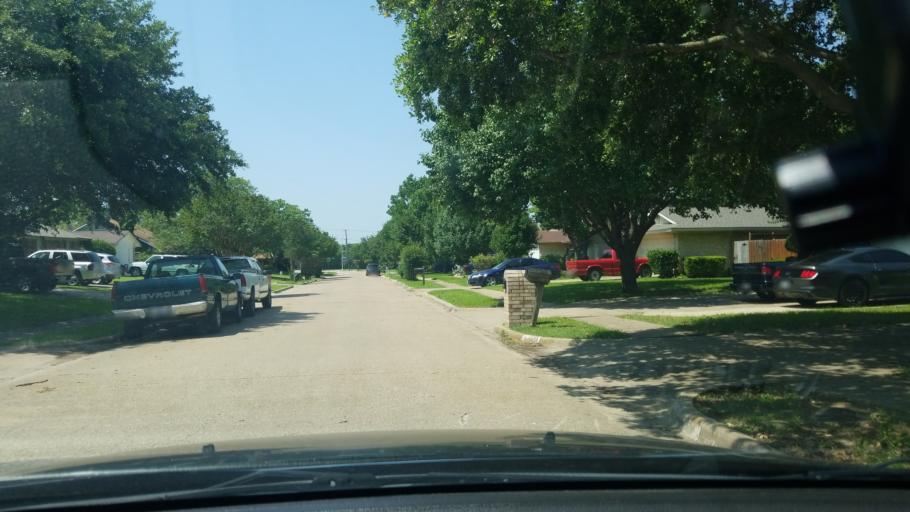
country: US
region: Texas
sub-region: Dallas County
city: Sunnyvale
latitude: 32.8262
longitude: -96.6064
